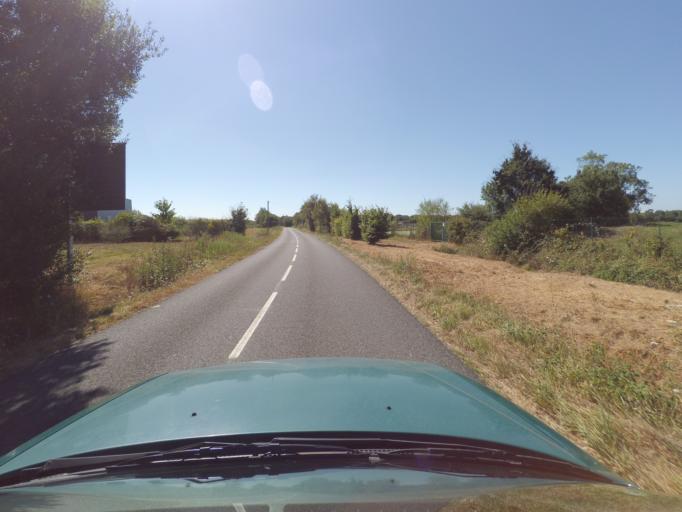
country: FR
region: Pays de la Loire
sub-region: Departement de la Loire-Atlantique
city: Le Bignon
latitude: 47.1183
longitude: -1.5046
